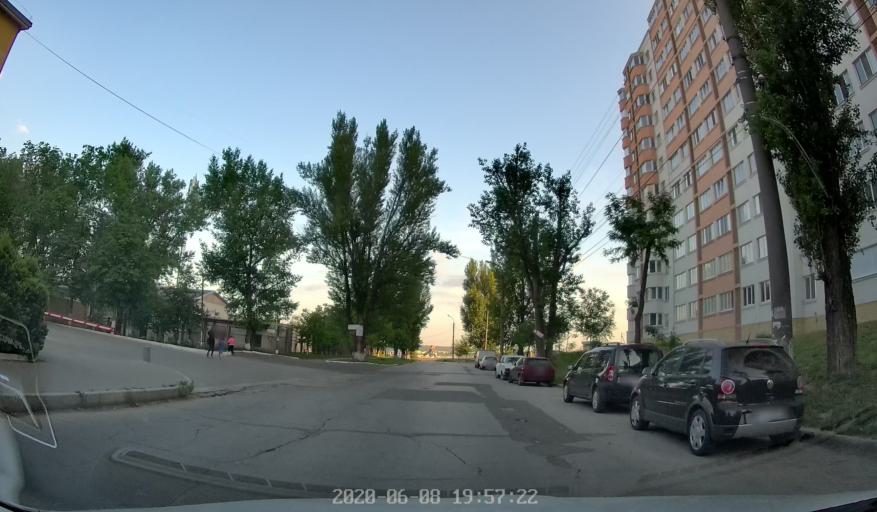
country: MD
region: Chisinau
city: Chisinau
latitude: 47.0162
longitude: 28.8825
